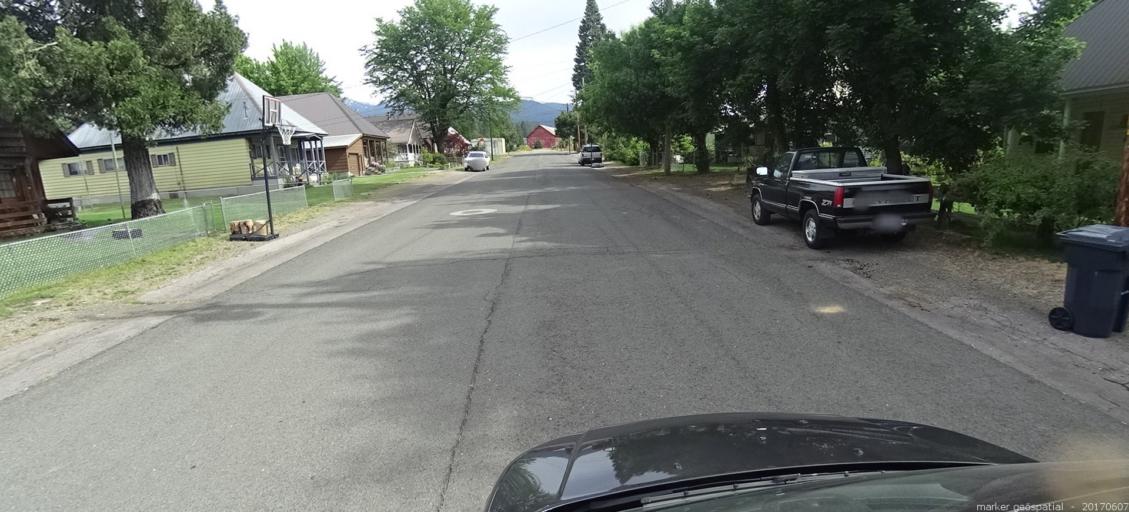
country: US
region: California
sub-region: Siskiyou County
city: McCloud
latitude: 41.2570
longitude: -122.1379
